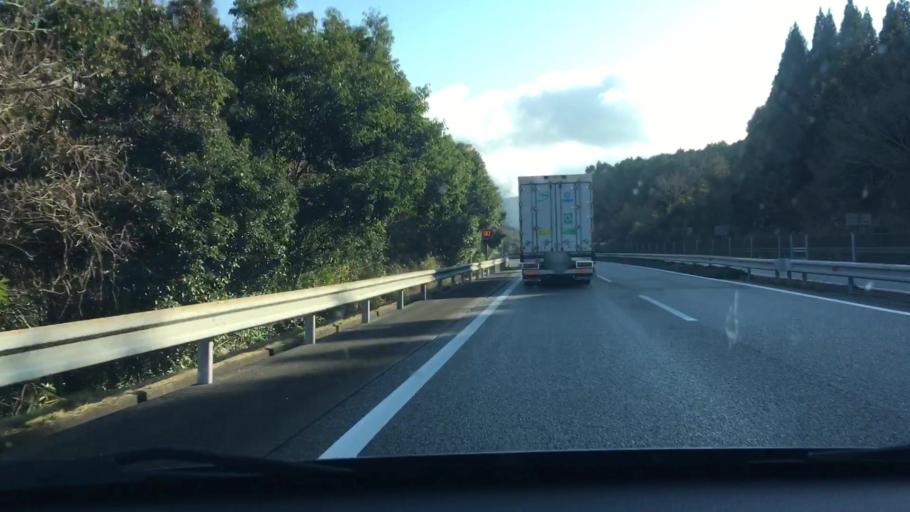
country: JP
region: Kumamoto
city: Hitoyoshi
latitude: 32.1672
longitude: 130.7930
